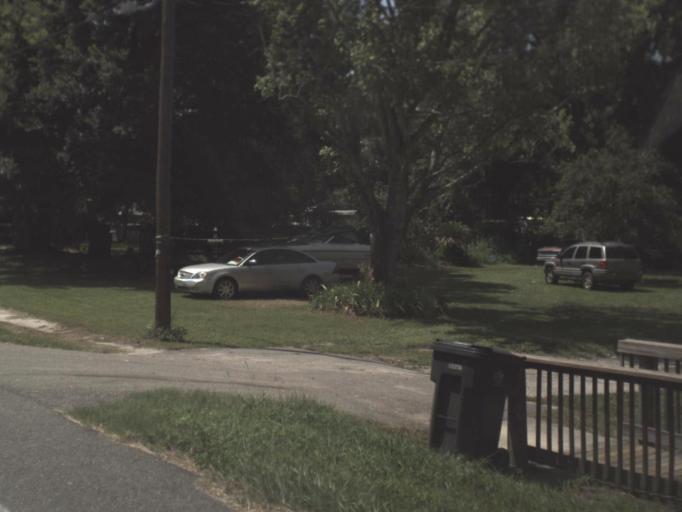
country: US
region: Florida
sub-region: Hillsborough County
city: Dover
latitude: 28.0208
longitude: -82.1844
